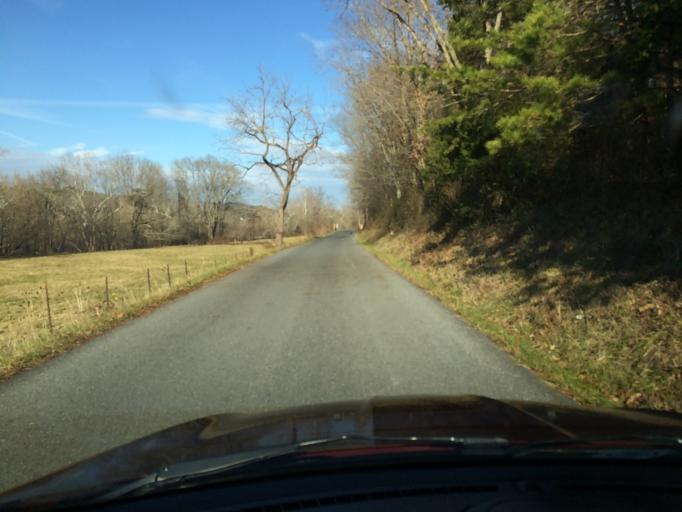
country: US
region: Virginia
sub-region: Alleghany County
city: Clifton Forge
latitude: 37.7464
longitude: -79.8170
